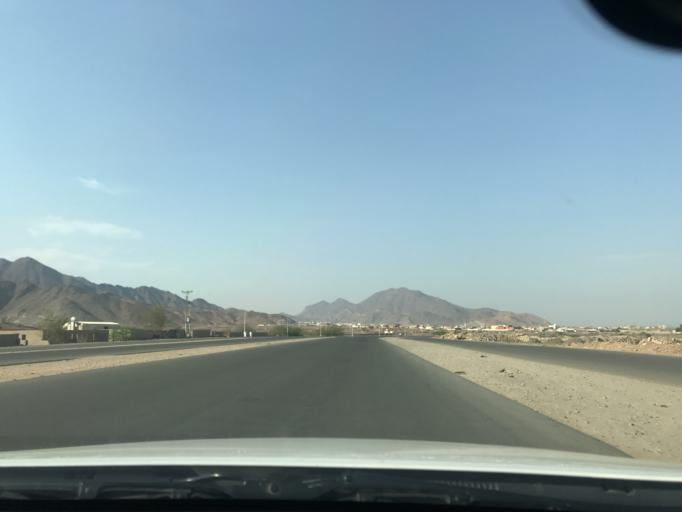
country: SA
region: Makkah
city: Al Jumum
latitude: 21.4481
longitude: 39.5206
